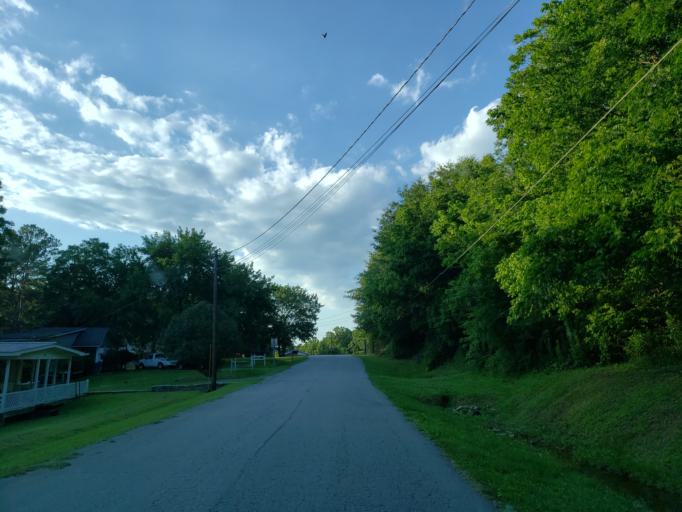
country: US
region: Georgia
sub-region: Haralson County
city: Tallapoosa
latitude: 33.7530
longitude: -85.2974
